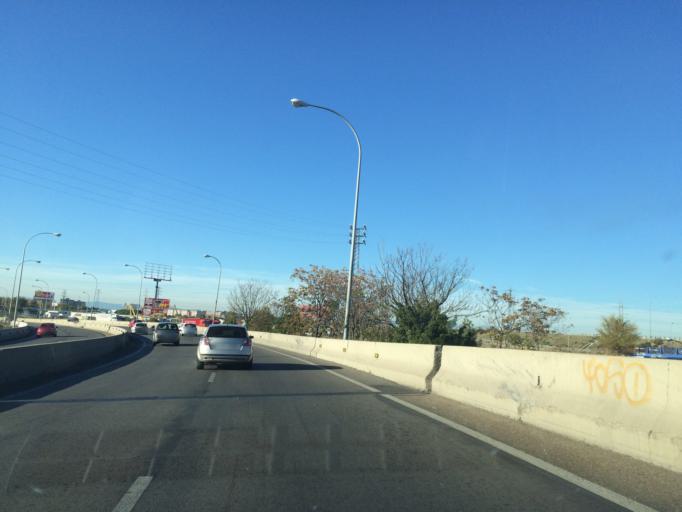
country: ES
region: Madrid
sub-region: Provincia de Madrid
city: Mostoles
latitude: 40.3239
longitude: -3.8436
